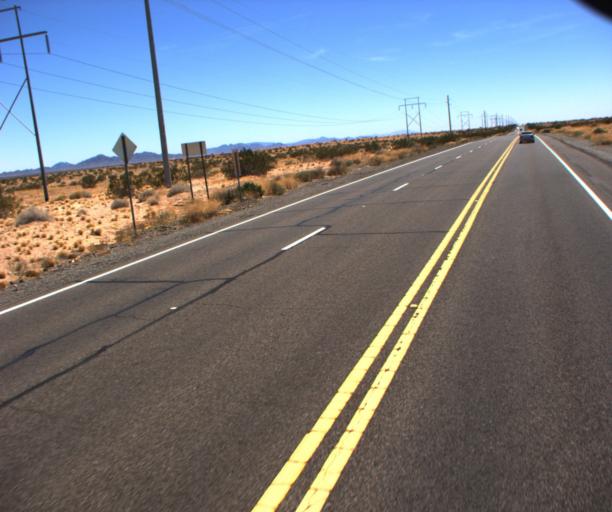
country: US
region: Arizona
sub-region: La Paz County
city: Parker
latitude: 33.9567
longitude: -114.2169
